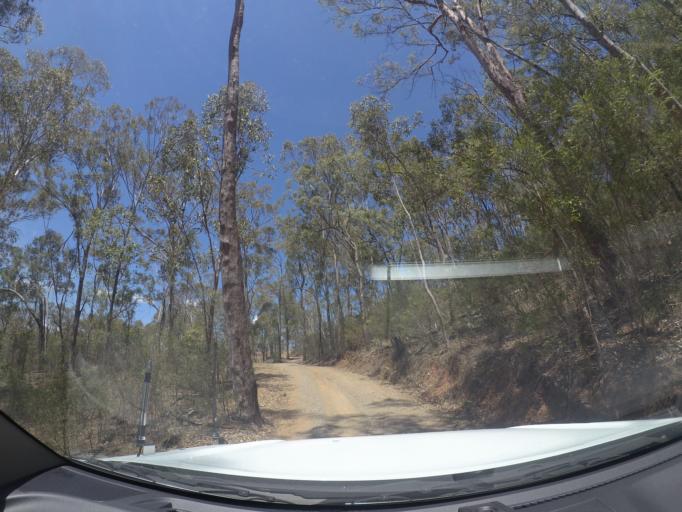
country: AU
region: Queensland
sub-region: Ipswich
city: Deebing Heights
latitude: -27.8316
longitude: 152.8265
